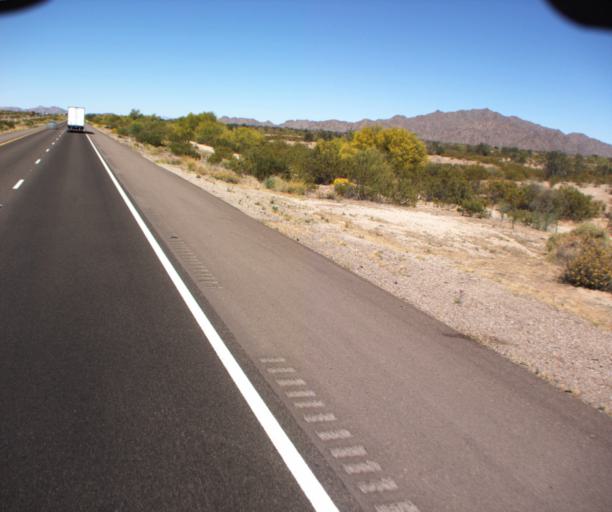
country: US
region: Arizona
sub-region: Maricopa County
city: Gila Bend
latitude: 33.1093
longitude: -112.6495
